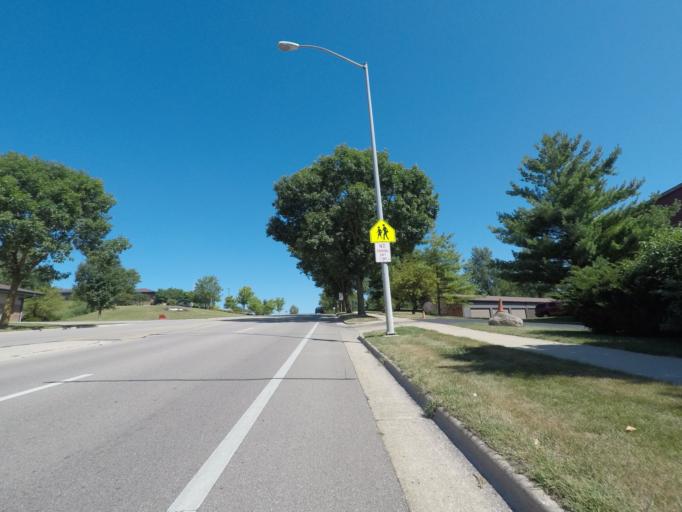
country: US
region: Wisconsin
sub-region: Dane County
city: Verona
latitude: 43.0328
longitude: -89.4968
